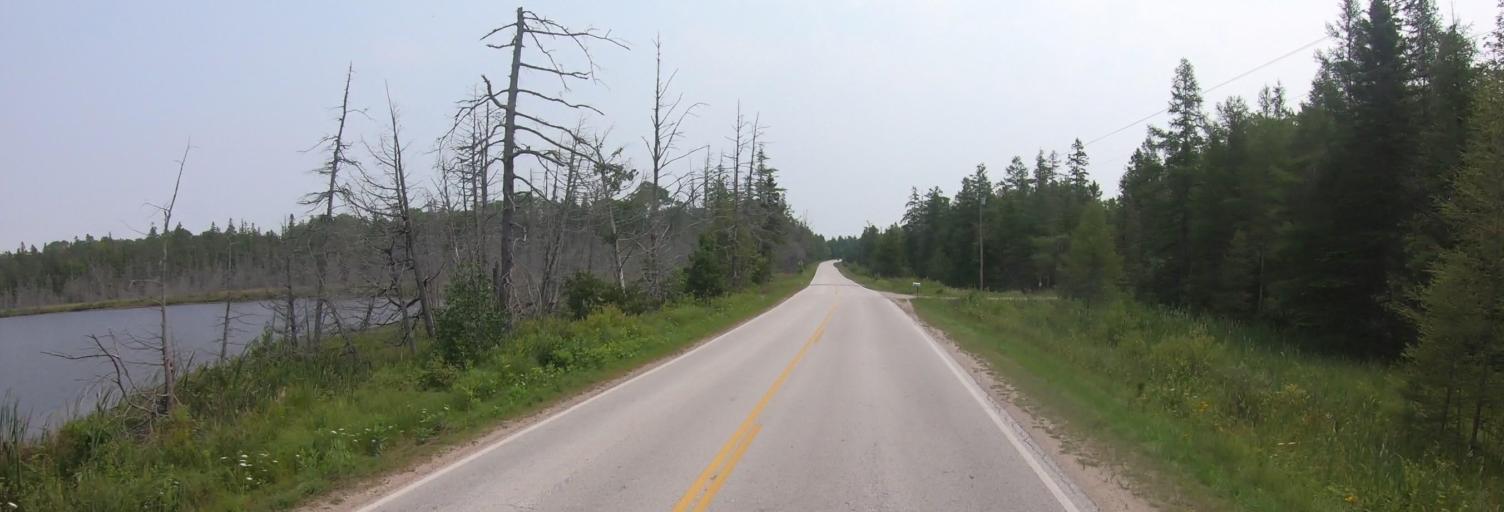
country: CA
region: Ontario
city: Thessalon
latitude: 45.9846
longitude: -83.6847
